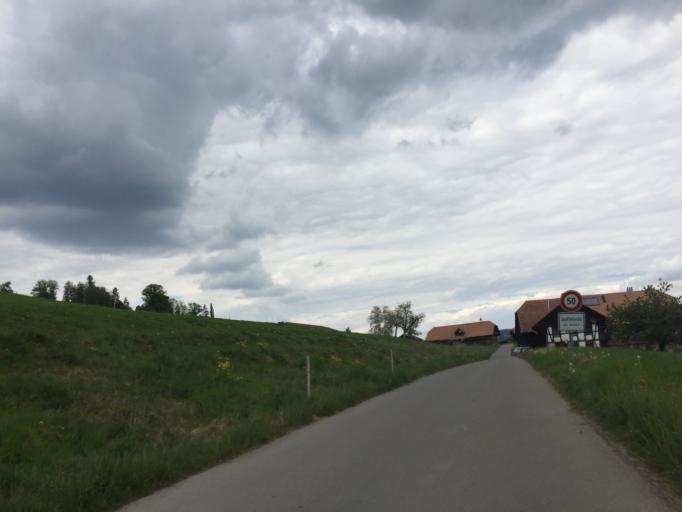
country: CH
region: Bern
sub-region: Thun District
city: Seftigen
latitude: 46.7967
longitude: 7.5551
